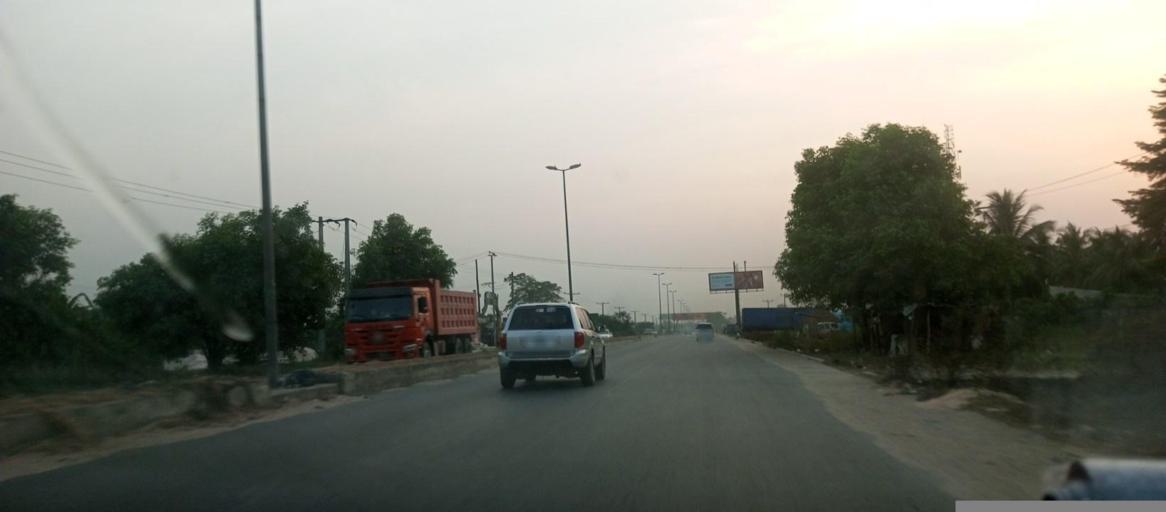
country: NG
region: Rivers
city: Emuoha
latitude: 4.9331
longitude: 7.0038
